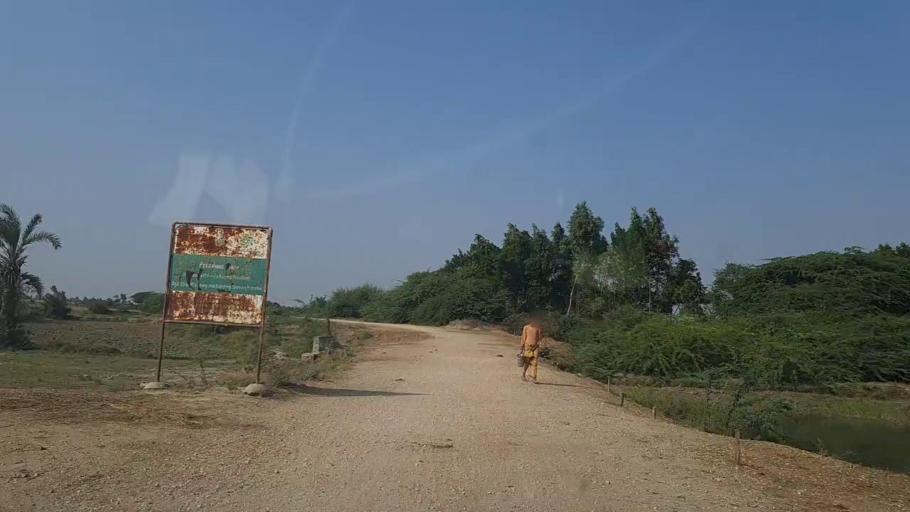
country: PK
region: Sindh
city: Mirpur Sakro
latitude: 24.5629
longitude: 67.8296
